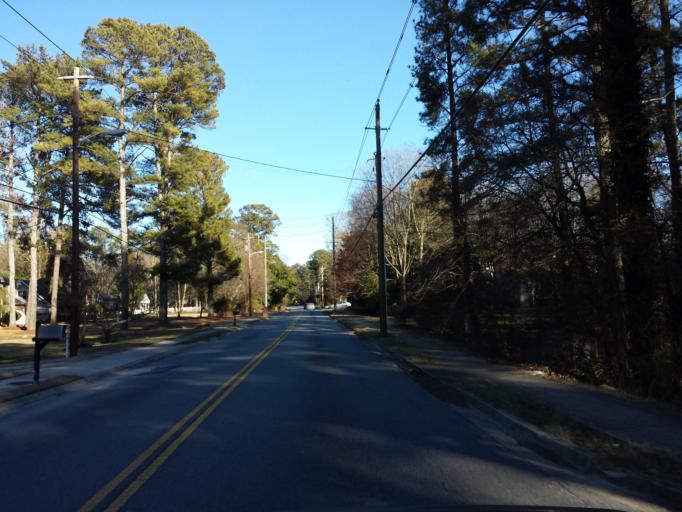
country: US
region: Georgia
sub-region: Cobb County
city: Smyrna
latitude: 33.9423
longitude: -84.4734
